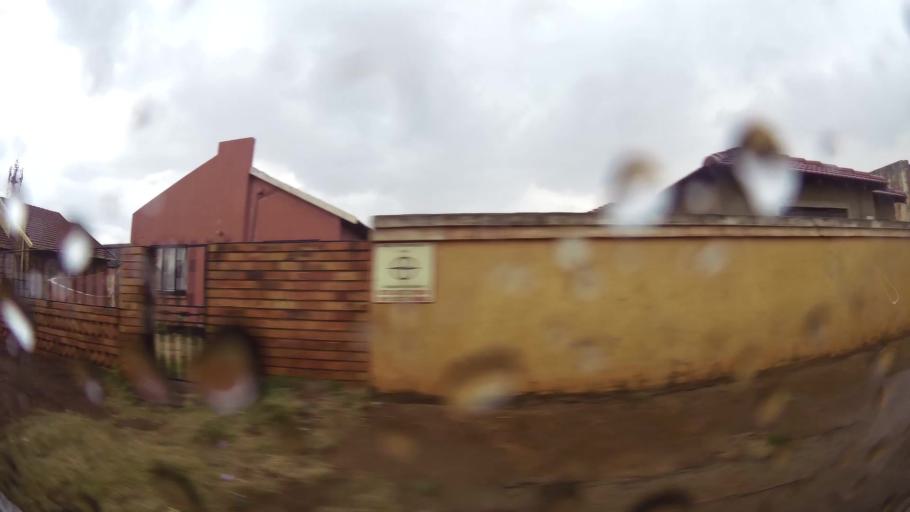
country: ZA
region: Gauteng
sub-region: Ekurhuleni Metropolitan Municipality
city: Germiston
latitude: -26.3651
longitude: 28.1324
